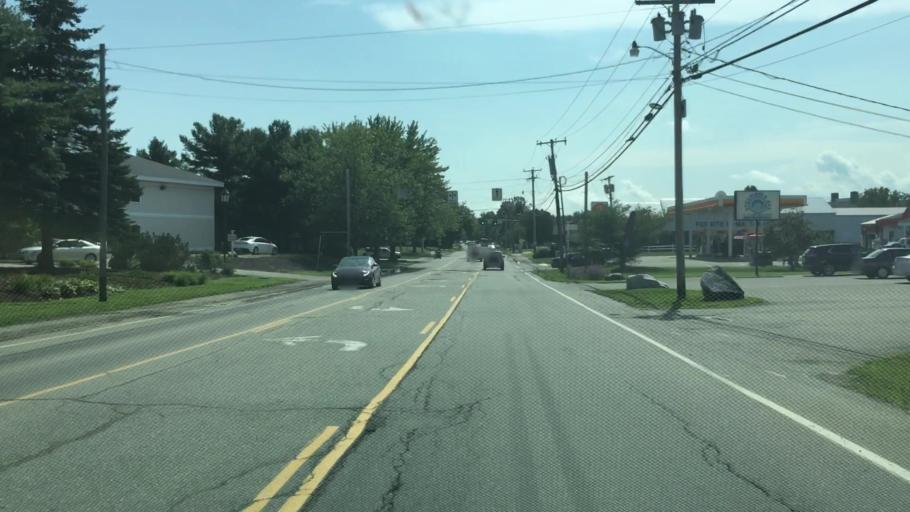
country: US
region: Maine
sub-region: Penobscot County
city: Brewer
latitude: 44.8227
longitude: -68.7601
